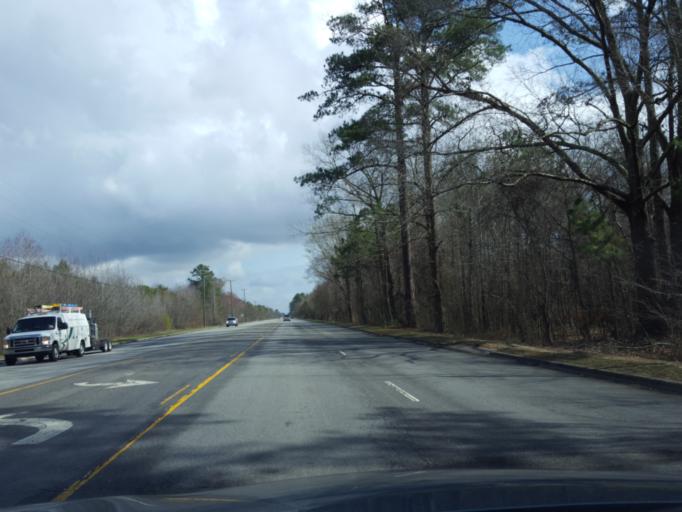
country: US
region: North Carolina
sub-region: Washington County
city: Plymouth
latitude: 35.8682
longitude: -76.7170
